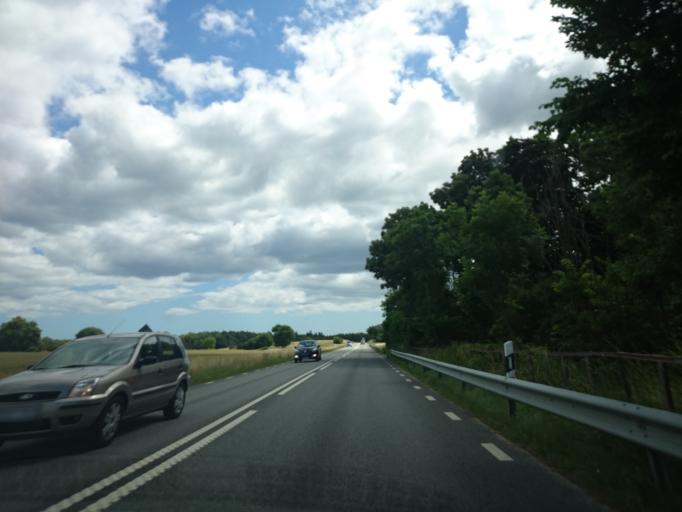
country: SE
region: Skane
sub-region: Kristianstads Kommun
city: Degeberga
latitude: 55.8199
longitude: 14.1221
